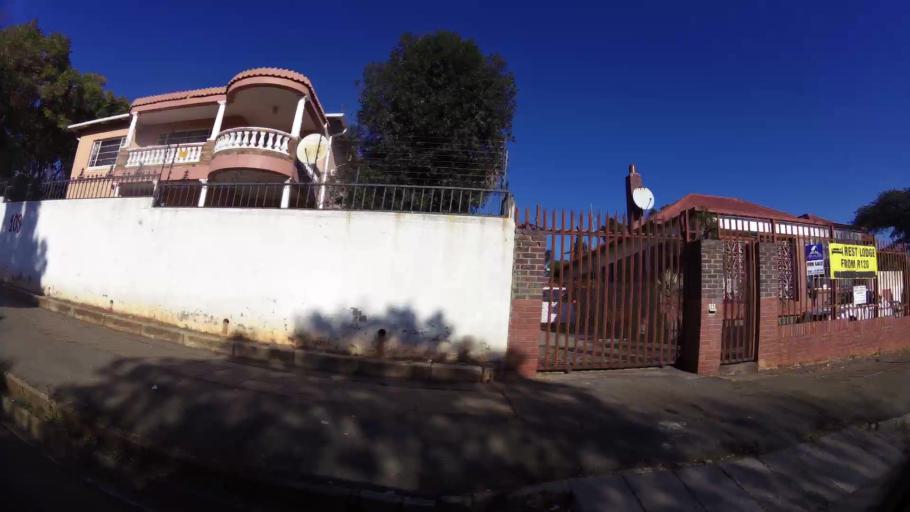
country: ZA
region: Gauteng
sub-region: City of Johannesburg Metropolitan Municipality
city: Johannesburg
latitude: -26.1925
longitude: 28.1101
